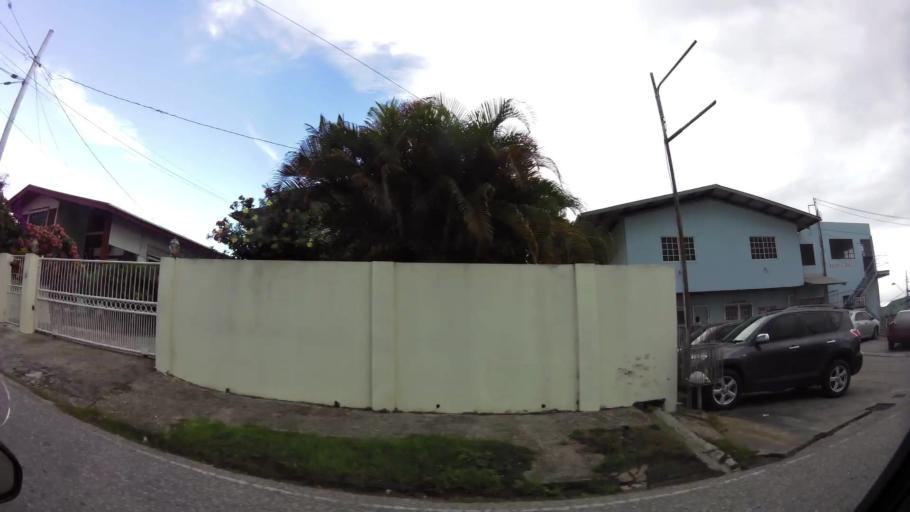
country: TT
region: Penal/Debe
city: Debe
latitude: 10.2431
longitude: -61.4424
